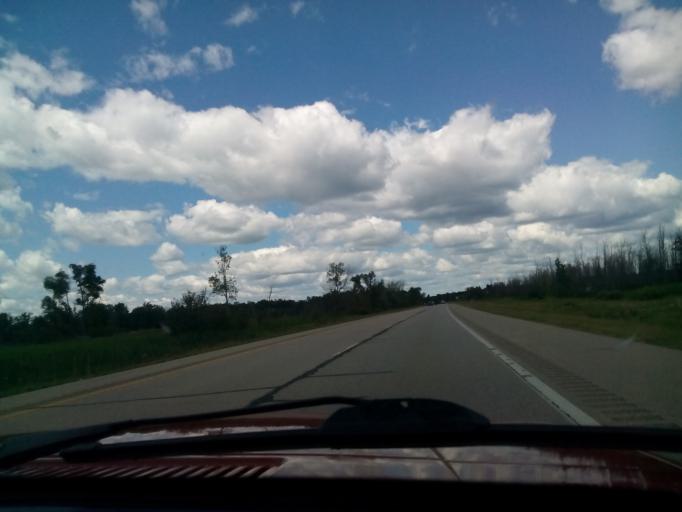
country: US
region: Michigan
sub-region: Ogemaw County
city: Skidway Lake
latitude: 44.0892
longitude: -84.1055
